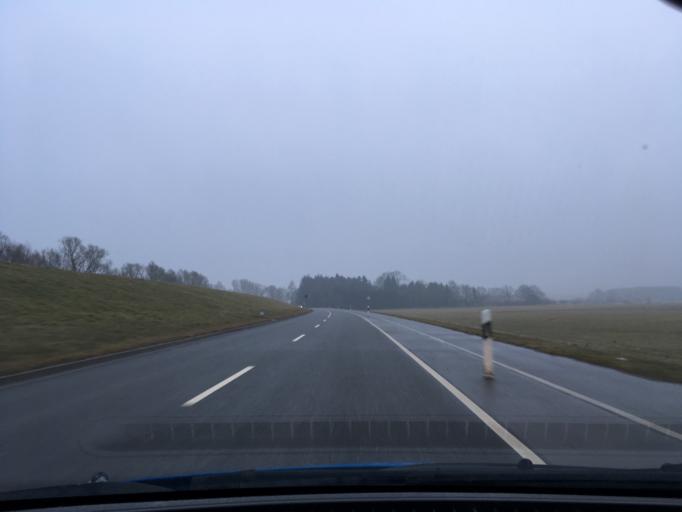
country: DE
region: Lower Saxony
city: Stelle
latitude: 53.4266
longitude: 10.1006
